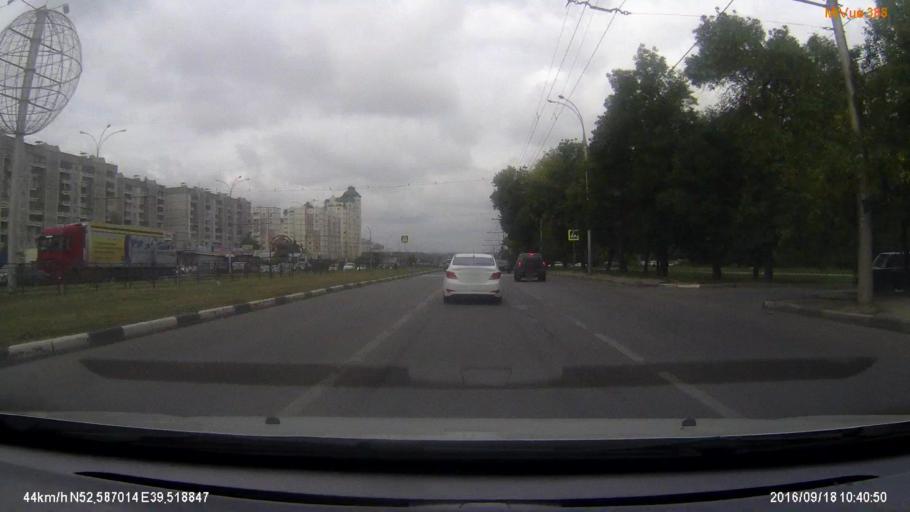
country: RU
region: Lipetsk
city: Syrskoye
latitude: 52.5866
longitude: 39.5193
